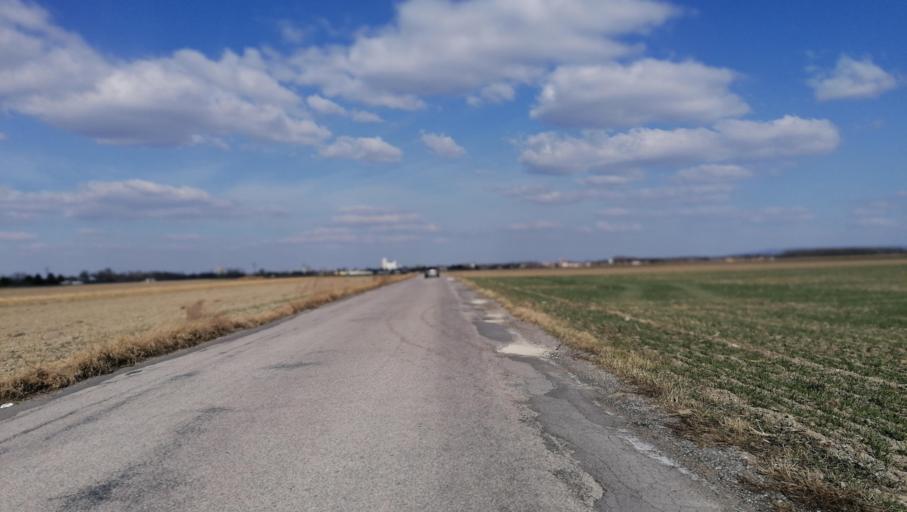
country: AT
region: Lower Austria
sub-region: Politischer Bezirk Wiener Neustadt
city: Lichtenworth
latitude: 47.8188
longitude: 16.2714
